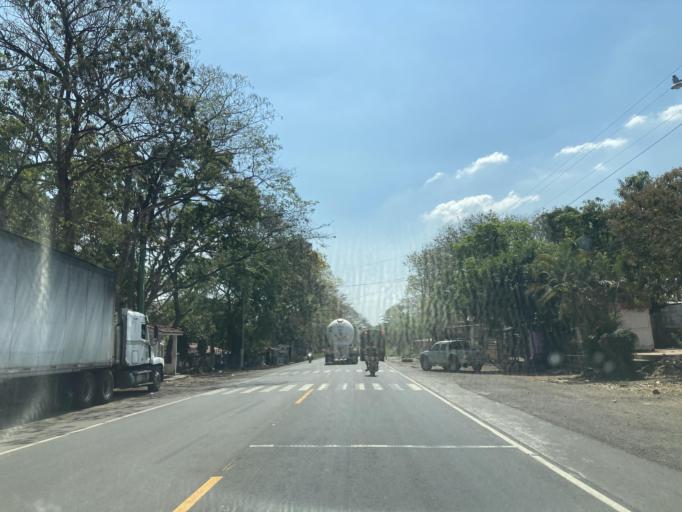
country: GT
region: Escuintla
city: Guanagazapa
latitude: 14.2232
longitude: -90.7309
